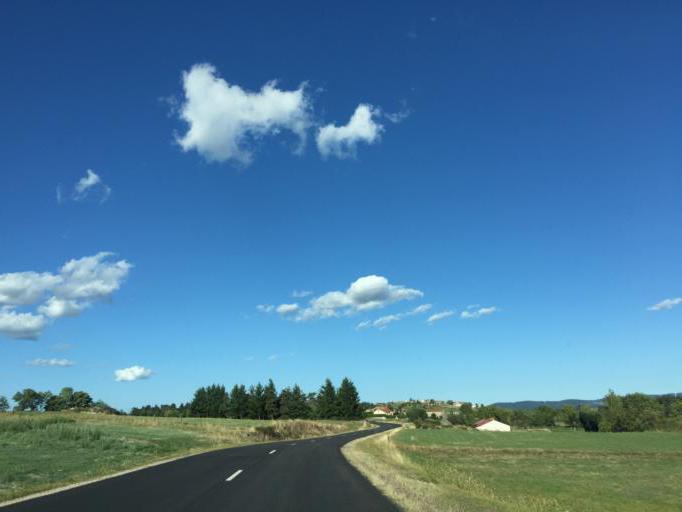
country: FR
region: Auvergne
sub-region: Departement de la Haute-Loire
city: Saugues
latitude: 44.9632
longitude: 3.5868
